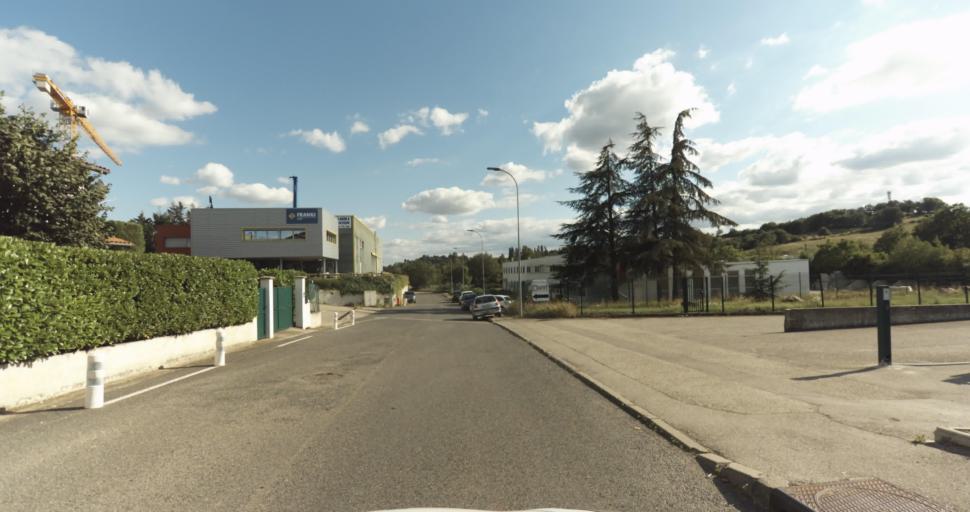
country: FR
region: Rhone-Alpes
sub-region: Departement du Rhone
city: Chaponost
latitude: 45.6954
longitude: 4.7647
